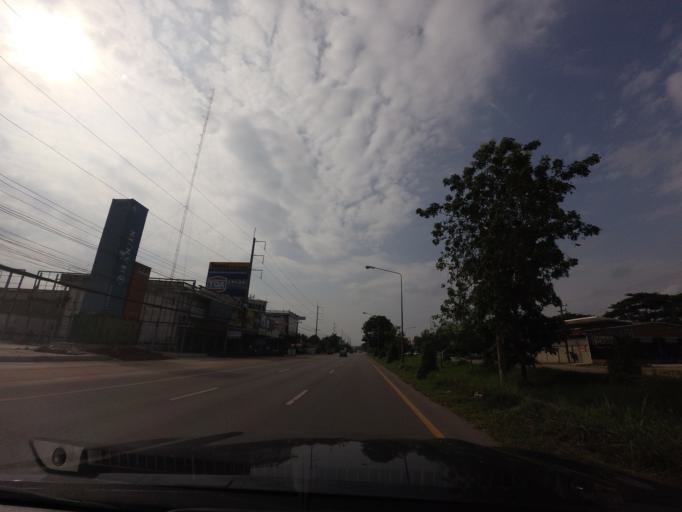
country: TH
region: Nong Khai
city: Nong Khai
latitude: 17.8526
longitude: 102.7508
